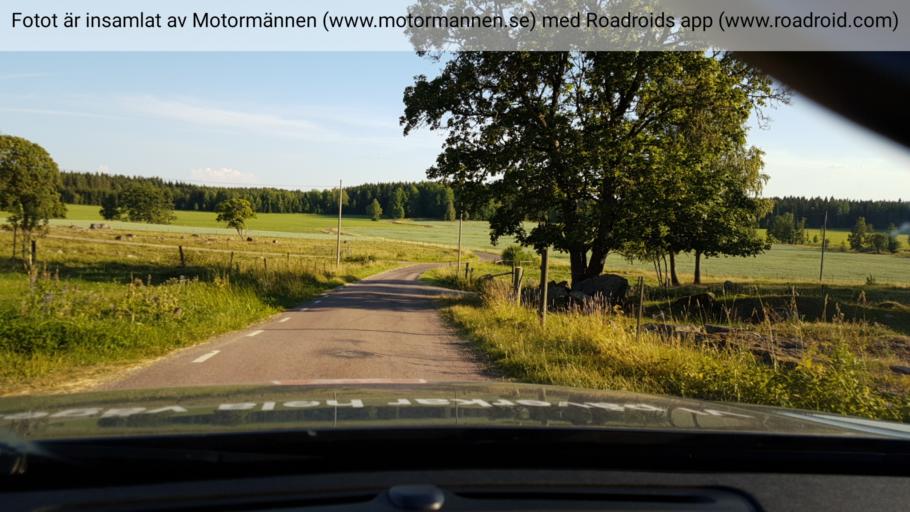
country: SE
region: Vaestmanland
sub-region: Surahammars Kommun
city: Surahammar
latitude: 59.6531
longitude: 16.0739
